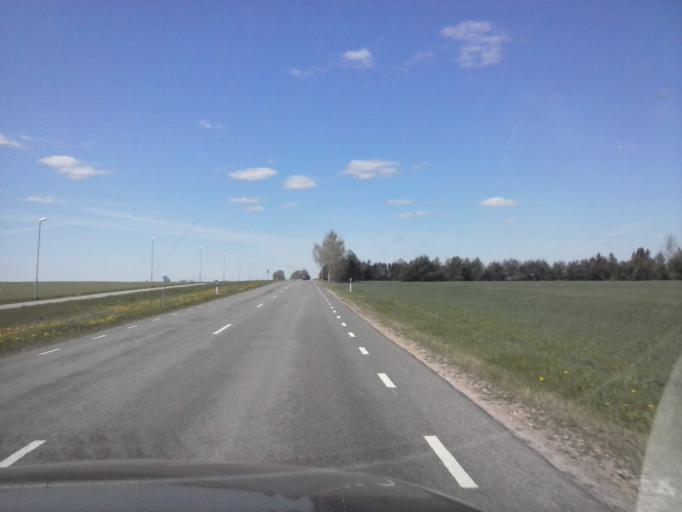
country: EE
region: Valgamaa
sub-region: Torva linn
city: Torva
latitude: 58.2183
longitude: 25.9052
